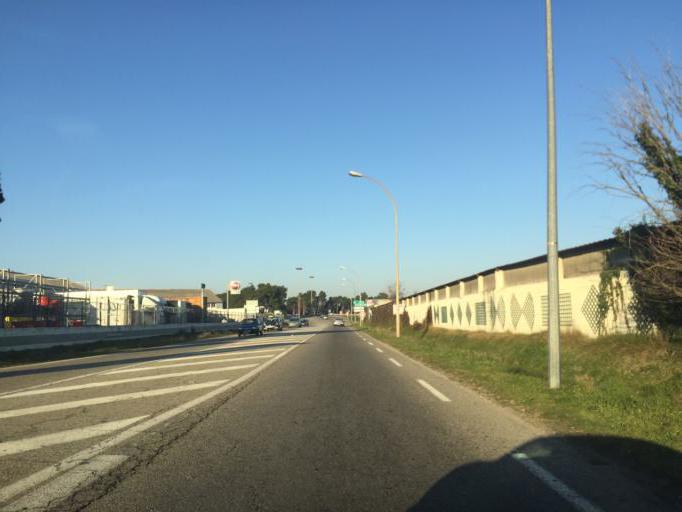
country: FR
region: Provence-Alpes-Cote d'Azur
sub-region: Departement du Vaucluse
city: Le Pontet
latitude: 43.9697
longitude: 4.8571
